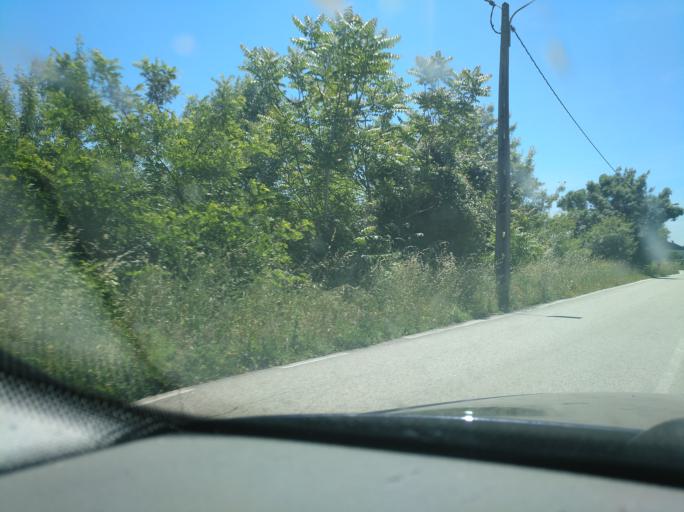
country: PT
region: Aveiro
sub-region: Mealhada
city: Pampilhosa do Botao
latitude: 40.2745
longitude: -8.4339
